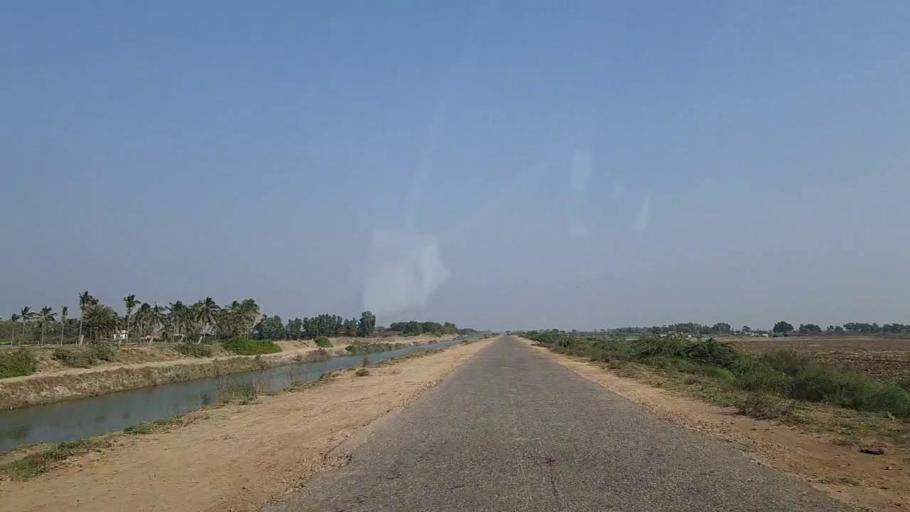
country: PK
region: Sindh
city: Mirpur Sakro
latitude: 24.6370
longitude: 67.5977
